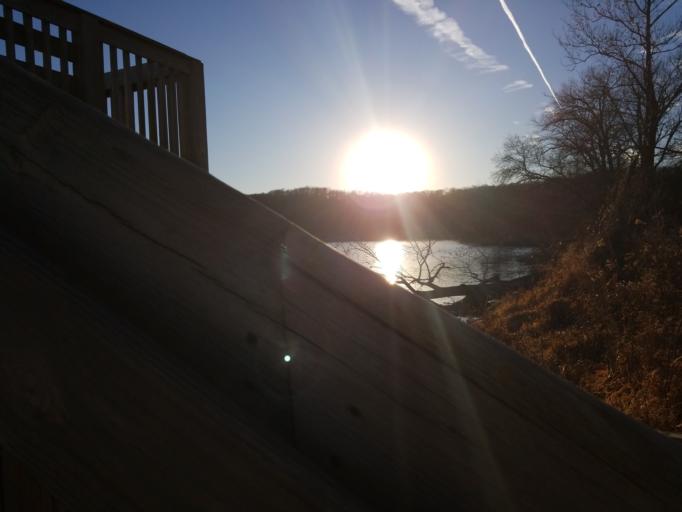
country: US
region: Nebraska
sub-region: Sarpy County
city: Bellevue
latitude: 41.1731
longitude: -95.8850
